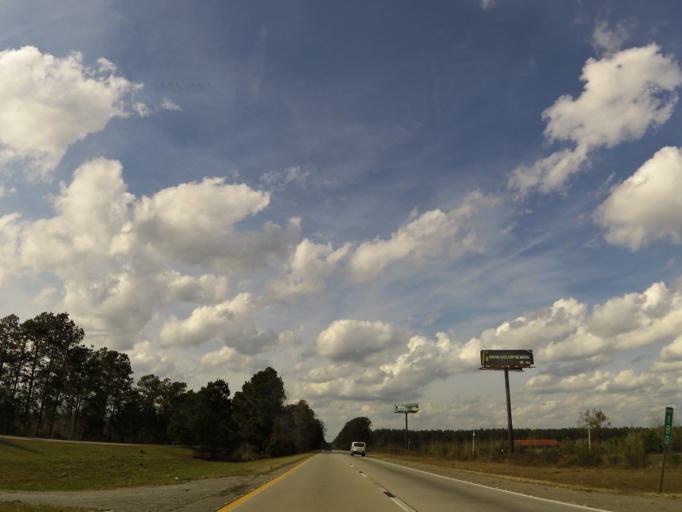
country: US
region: South Carolina
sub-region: Orangeburg County
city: Holly Hill
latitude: 33.2059
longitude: -80.4061
